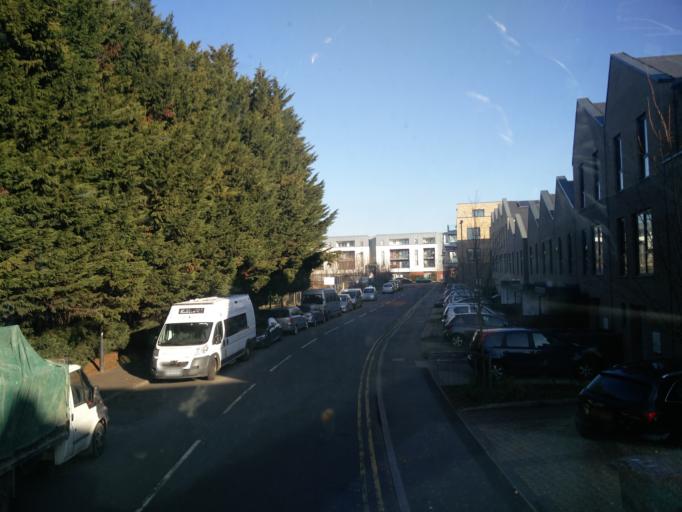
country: GB
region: England
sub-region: Greater London
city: Northolt
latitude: 51.5698
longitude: -0.3641
